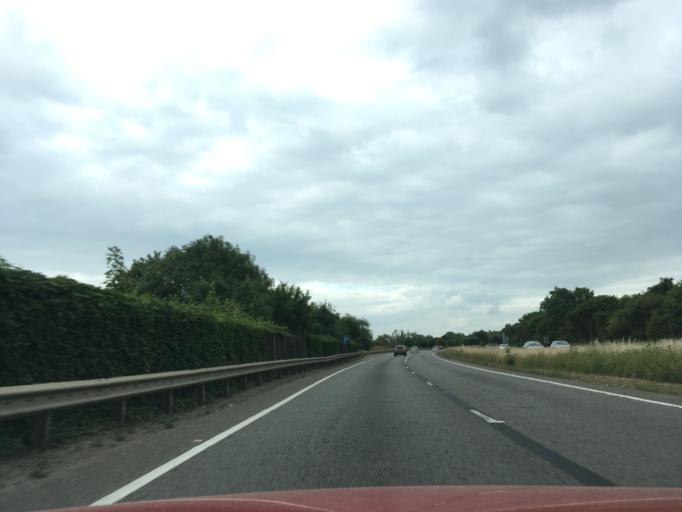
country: GB
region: England
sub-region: Buckinghamshire
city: Bletchley
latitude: 52.0133
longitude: -0.7275
